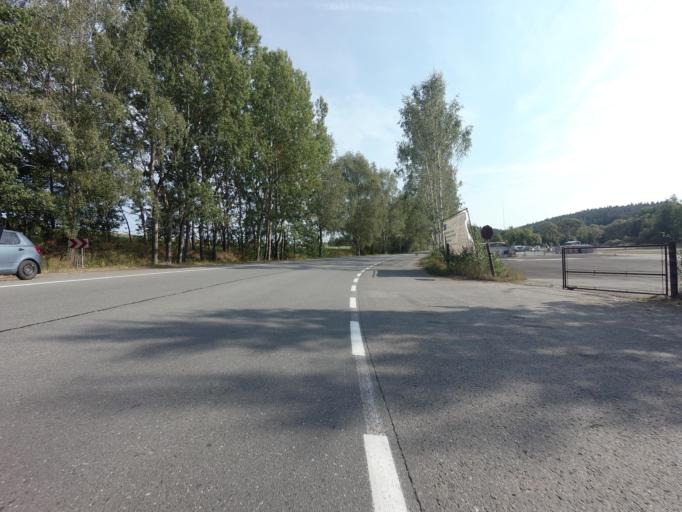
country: CZ
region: Jihocesky
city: Milevsko
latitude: 49.4726
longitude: 14.3620
